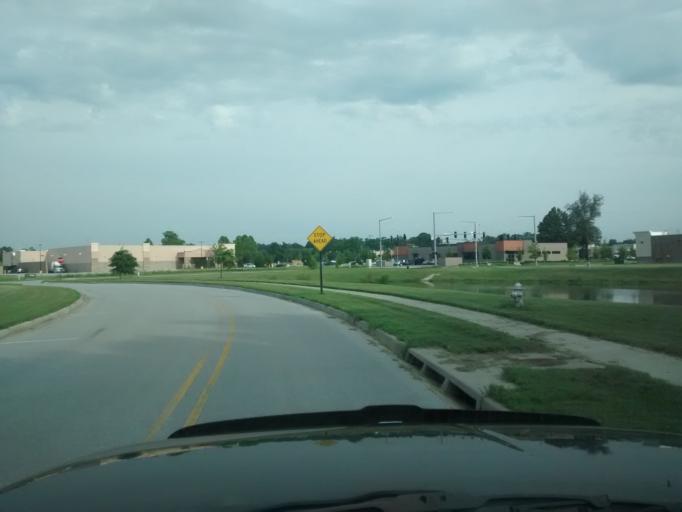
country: US
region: Arkansas
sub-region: Washington County
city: Farmington
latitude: 36.0754
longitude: -94.2078
